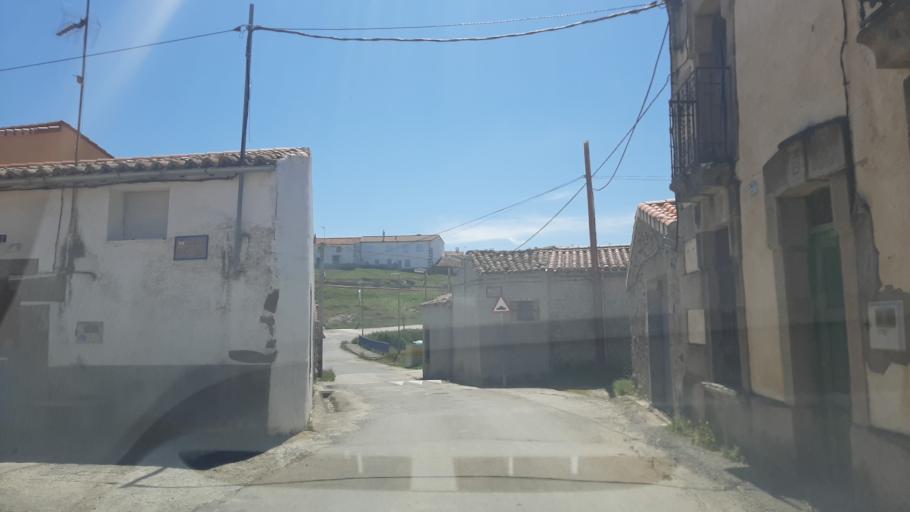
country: ES
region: Castille and Leon
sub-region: Provincia de Avila
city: Narrillos del Alamo
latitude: 40.5368
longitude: -5.4473
